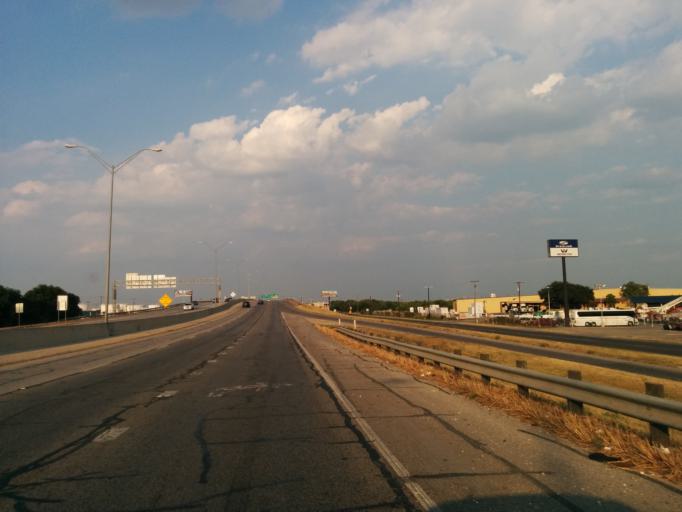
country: US
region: Texas
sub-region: Bexar County
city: Kirby
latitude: 29.4319
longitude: -98.4041
